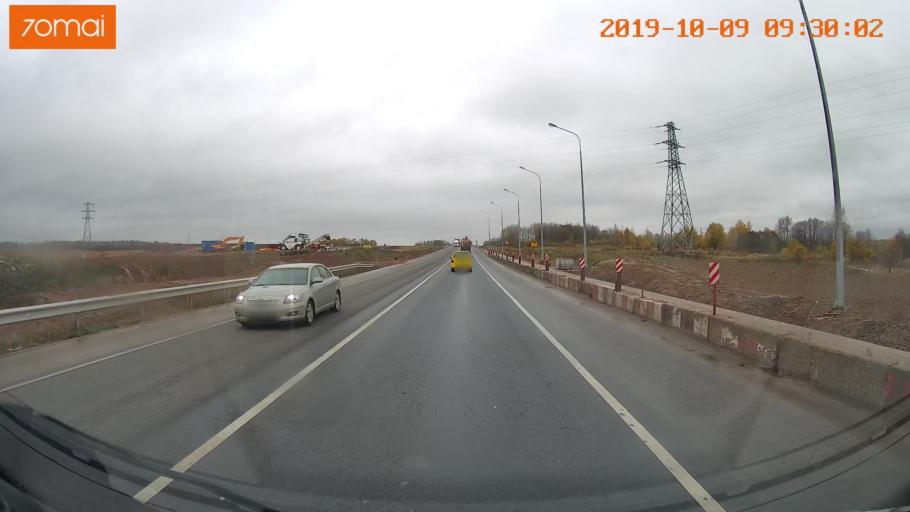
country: RU
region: Vologda
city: Vologda
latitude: 59.1366
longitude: 39.9527
